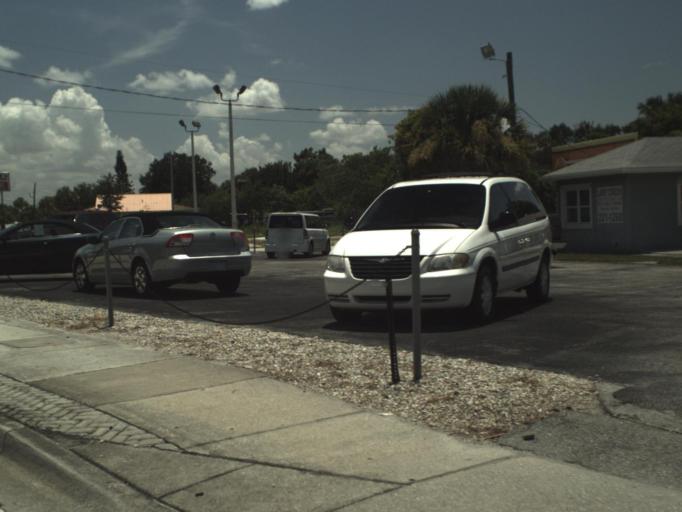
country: US
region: Florida
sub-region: Martin County
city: Stuart
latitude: 27.1952
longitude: -80.2571
